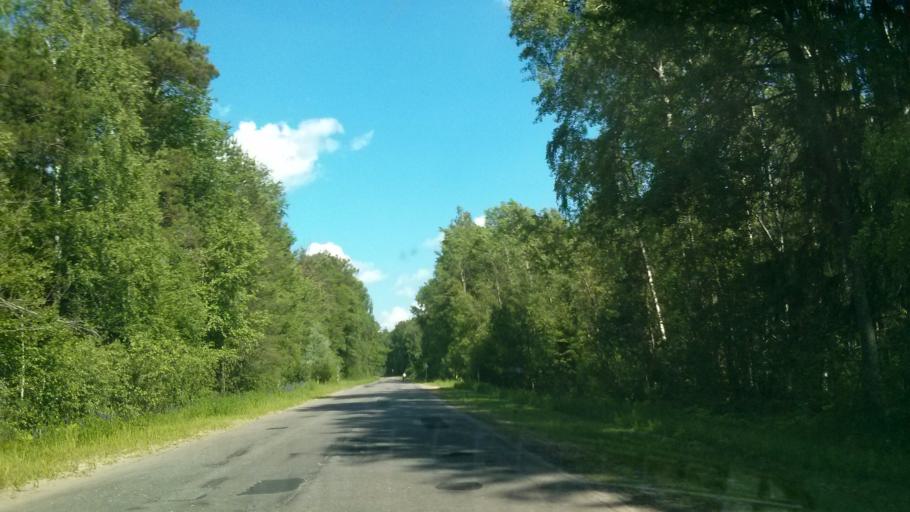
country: RU
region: Vladimir
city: Melenki
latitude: 55.3320
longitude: 41.6882
